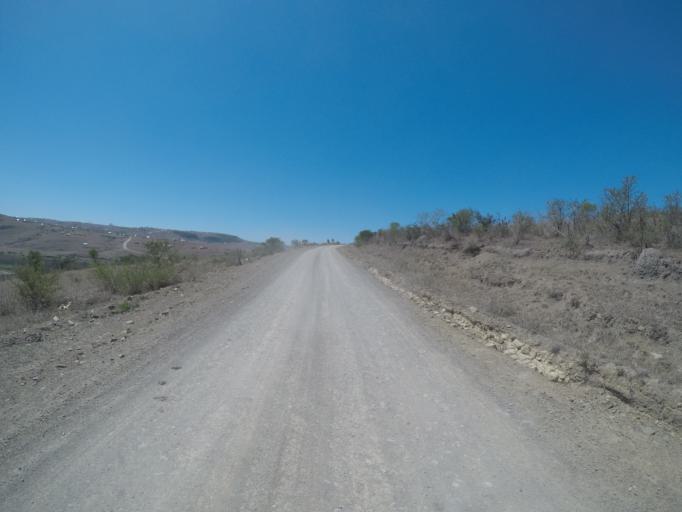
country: ZA
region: Eastern Cape
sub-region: OR Tambo District Municipality
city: Mthatha
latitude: -31.8732
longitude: 28.8699
